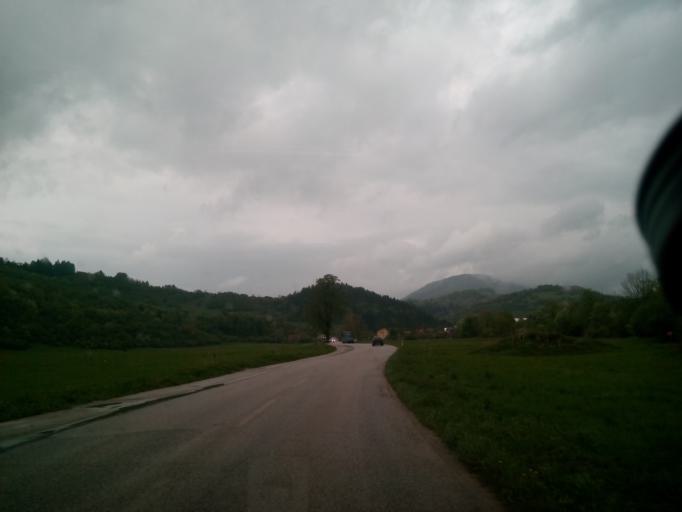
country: SK
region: Zilinsky
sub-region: Okres Zilina
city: Terchova
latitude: 49.2548
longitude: 19.0157
